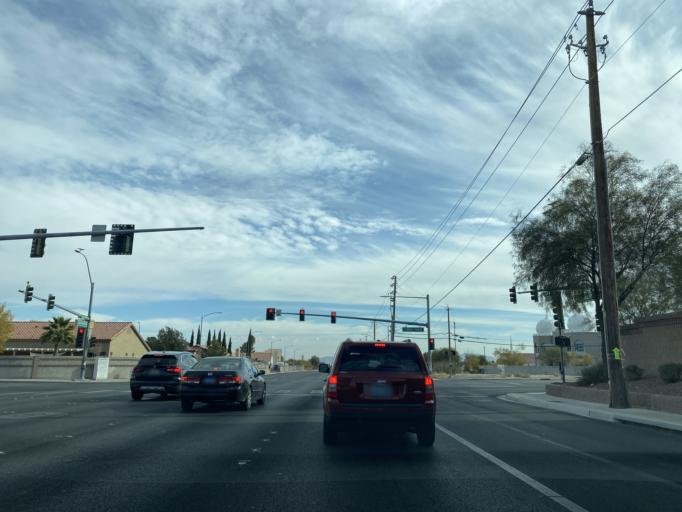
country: US
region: Nevada
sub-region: Clark County
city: Las Vegas
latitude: 36.2471
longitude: -115.2343
